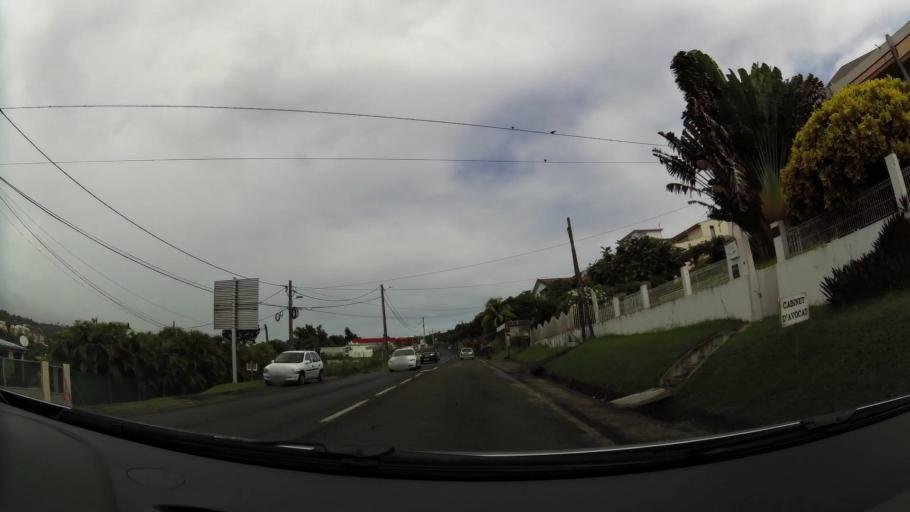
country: MQ
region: Martinique
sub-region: Martinique
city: Le Lamentin
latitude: 14.6226
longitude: -61.0189
